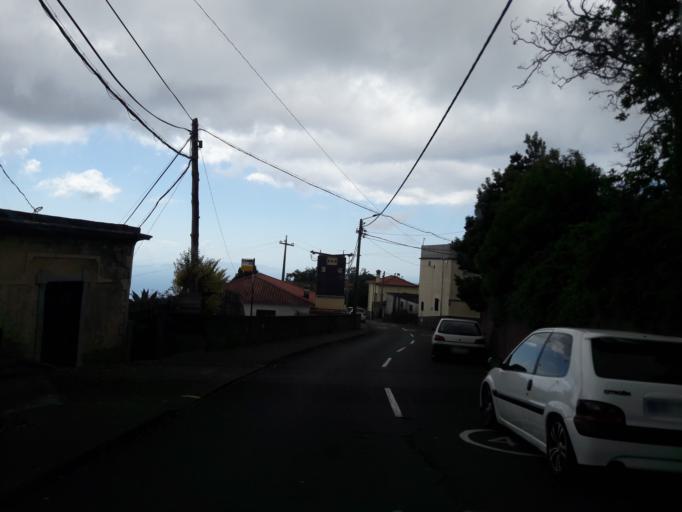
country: PT
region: Madeira
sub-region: Santa Cruz
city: Camacha
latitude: 32.6826
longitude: -16.8472
